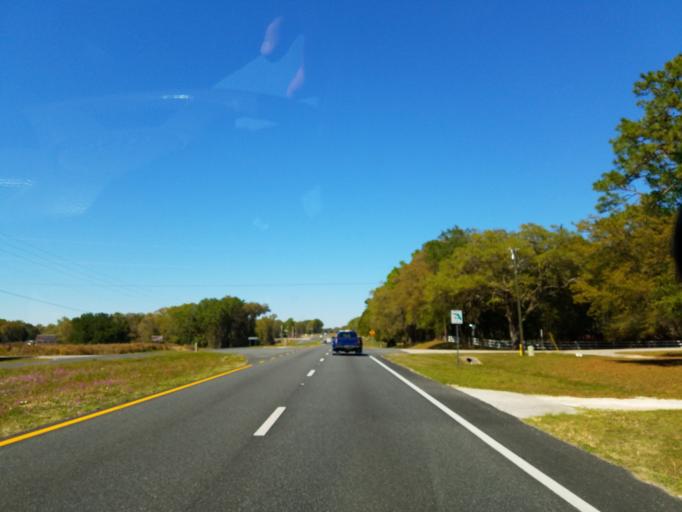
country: US
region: Florida
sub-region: Marion County
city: Belleview
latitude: 29.0253
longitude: -82.0449
